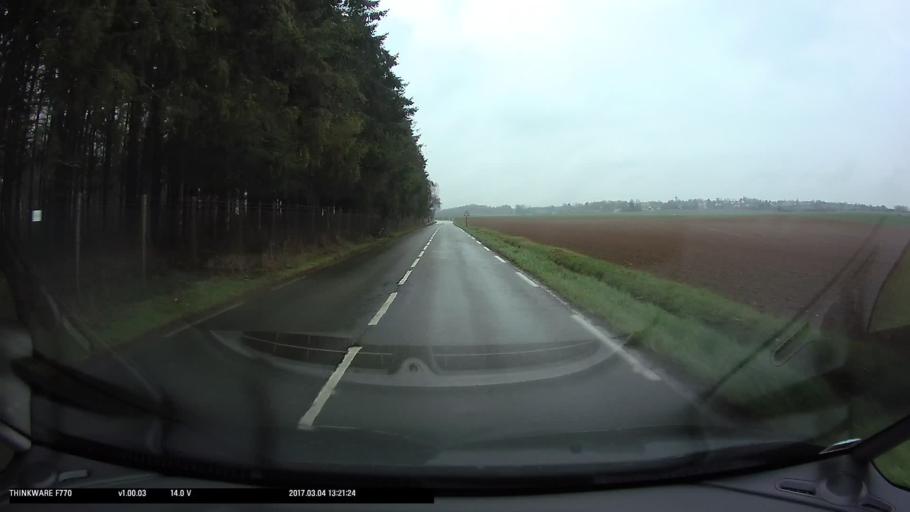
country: FR
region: Ile-de-France
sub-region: Departement du Val-d'Oise
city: Us
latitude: 49.1131
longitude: 1.9803
